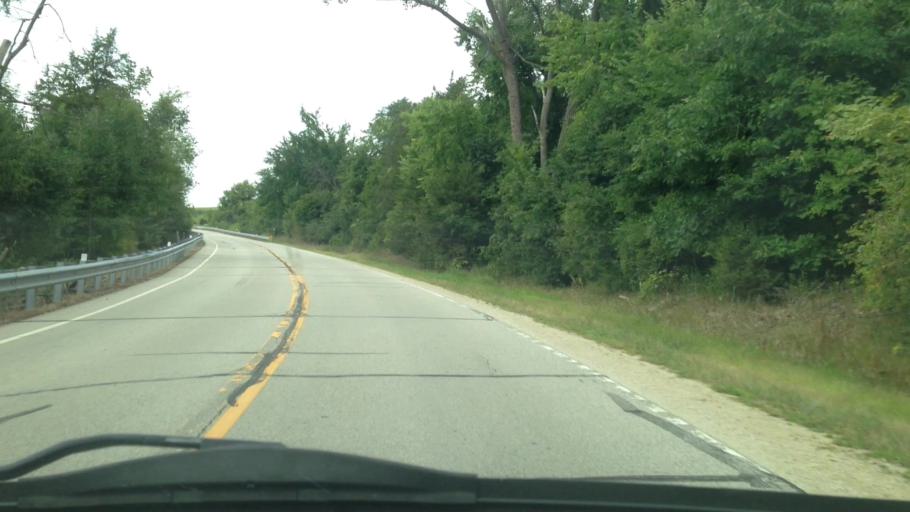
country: US
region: Minnesota
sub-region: Fillmore County
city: Preston
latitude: 43.7527
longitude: -91.9642
